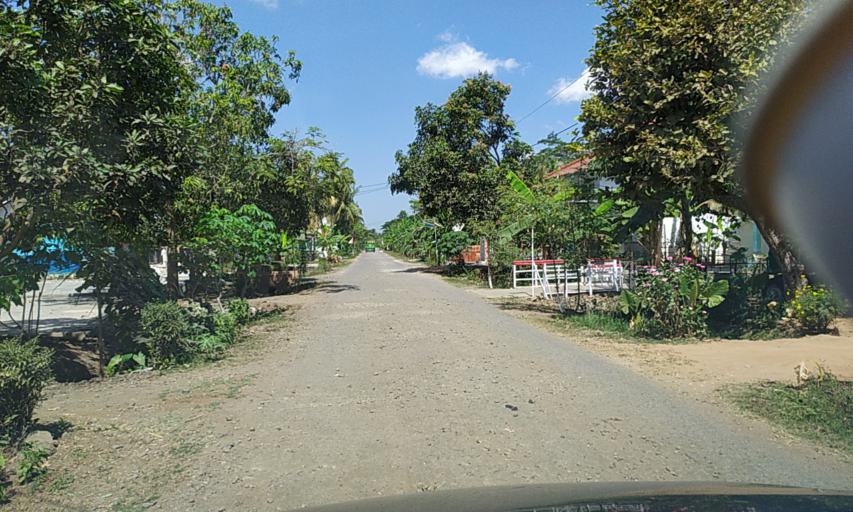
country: ID
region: Central Java
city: Kalenaren
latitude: -7.5815
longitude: 108.7894
